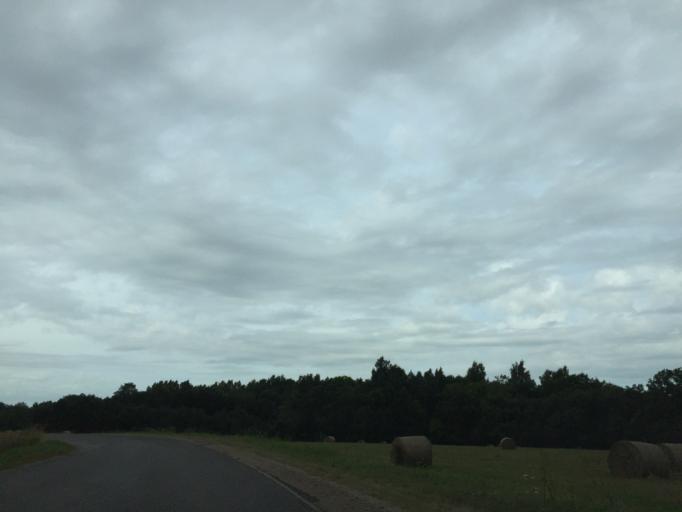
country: LV
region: Engure
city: Smarde
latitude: 56.7984
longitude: 23.2777
